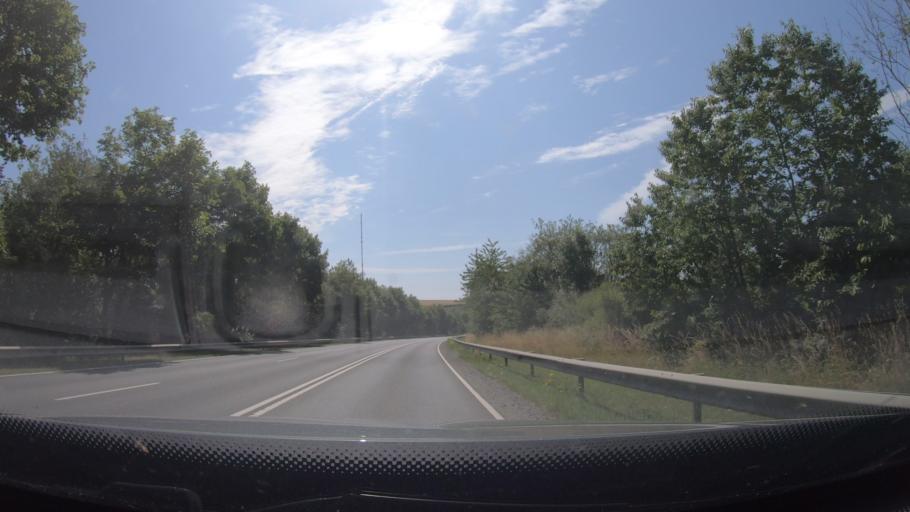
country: LU
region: Diekirch
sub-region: Canton de Clervaux
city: Hosingen
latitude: 50.0280
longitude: 6.0881
